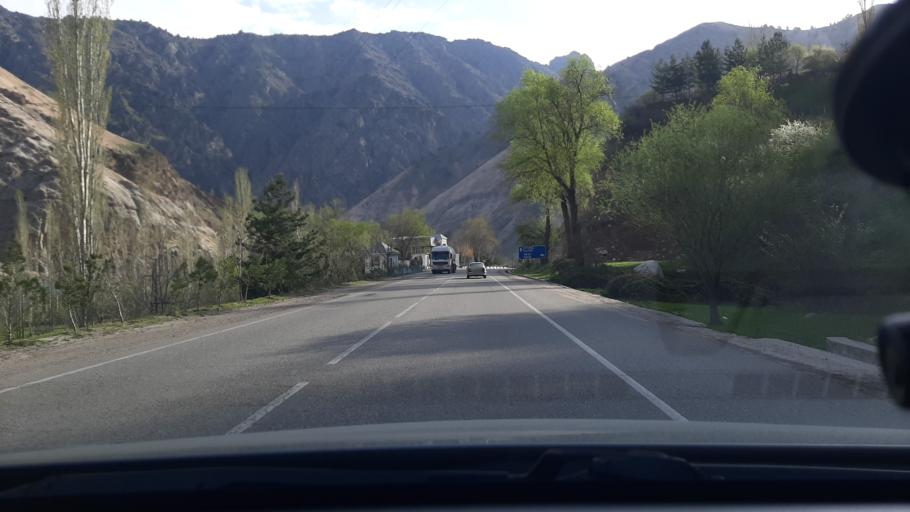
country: TJ
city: Tagob
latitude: 38.8460
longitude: 68.8447
